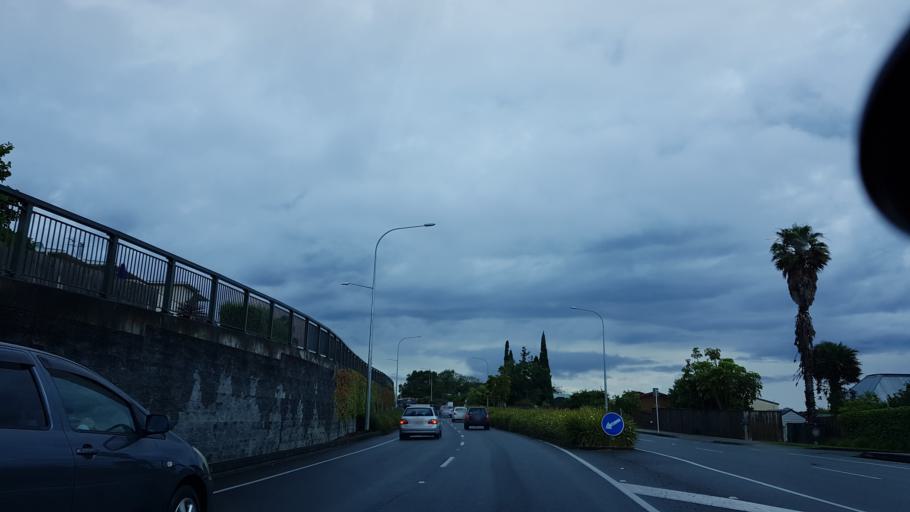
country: NZ
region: Auckland
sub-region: Auckland
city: North Shore
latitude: -36.7726
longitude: 174.7209
